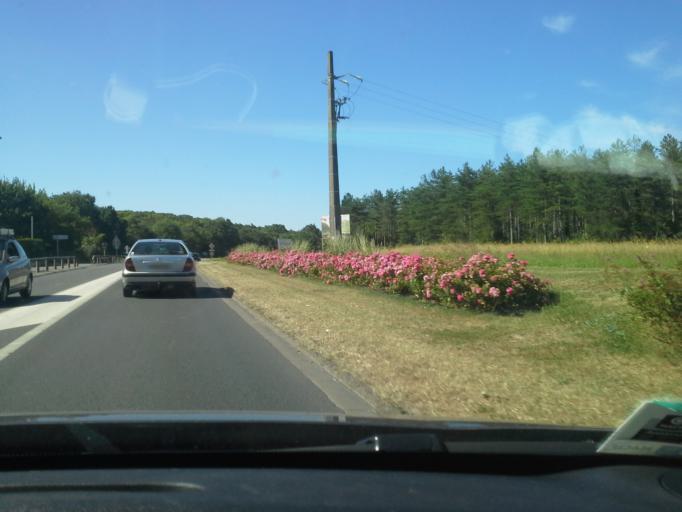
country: FR
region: Centre
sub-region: Departement du Loir-et-Cher
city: Cellettes
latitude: 47.5347
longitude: 1.3762
